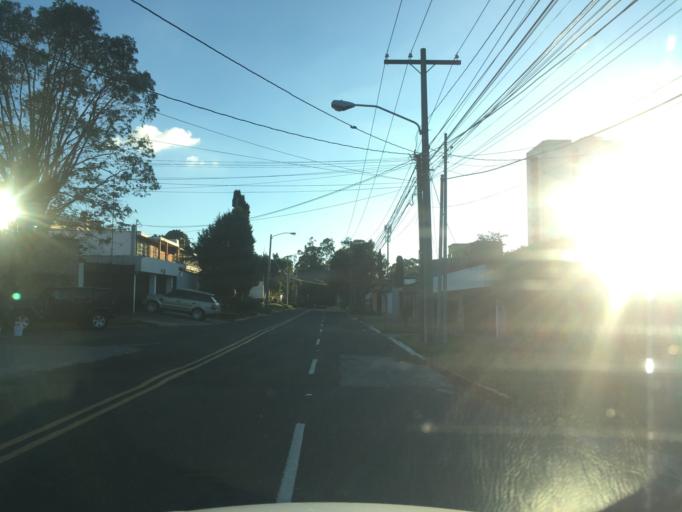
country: GT
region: Guatemala
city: Santa Catarina Pinula
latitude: 14.6042
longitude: -90.4875
